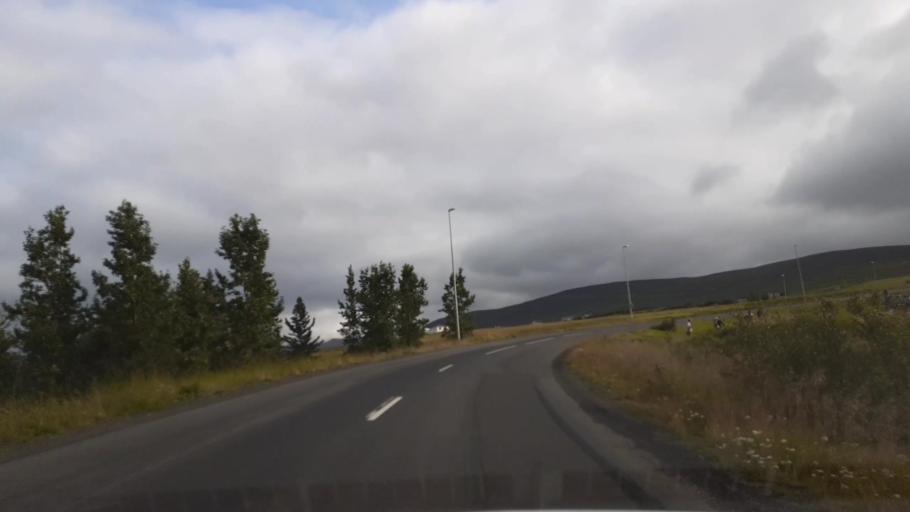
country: IS
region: Northeast
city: Akureyri
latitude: 65.7492
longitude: -18.0789
